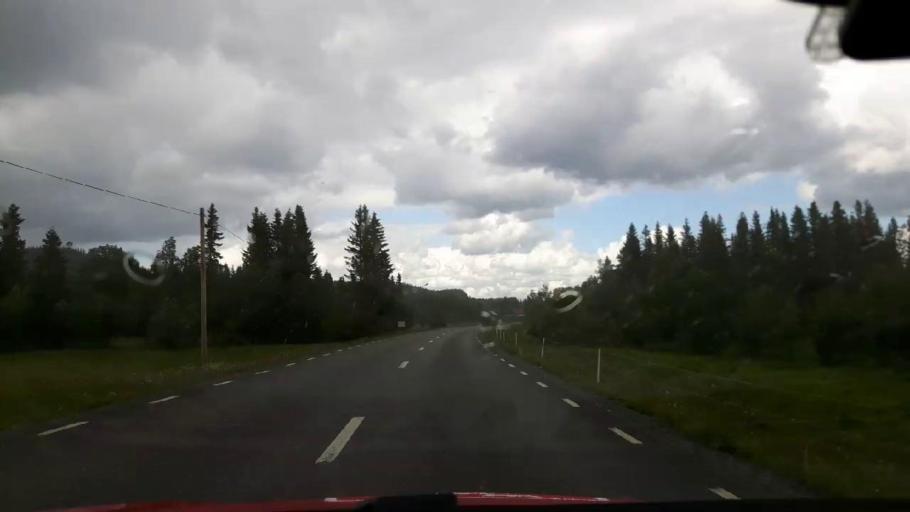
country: SE
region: Jaemtland
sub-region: Krokoms Kommun
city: Krokom
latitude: 63.7456
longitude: 14.2864
